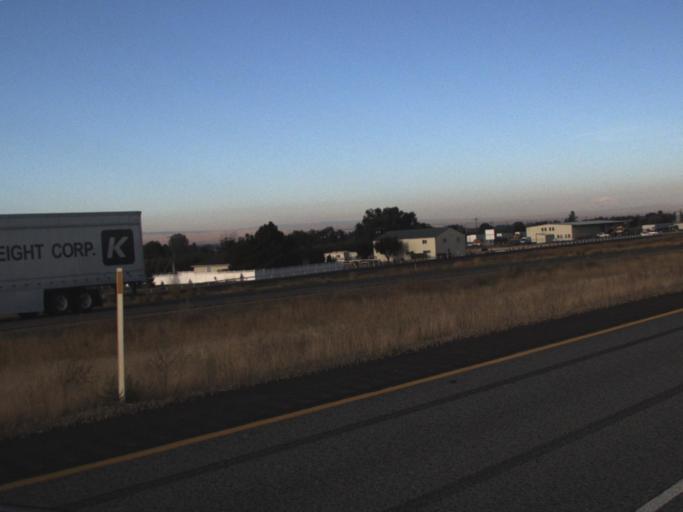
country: US
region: Washington
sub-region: Yakima County
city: Grandview
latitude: 46.2448
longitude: -119.8437
